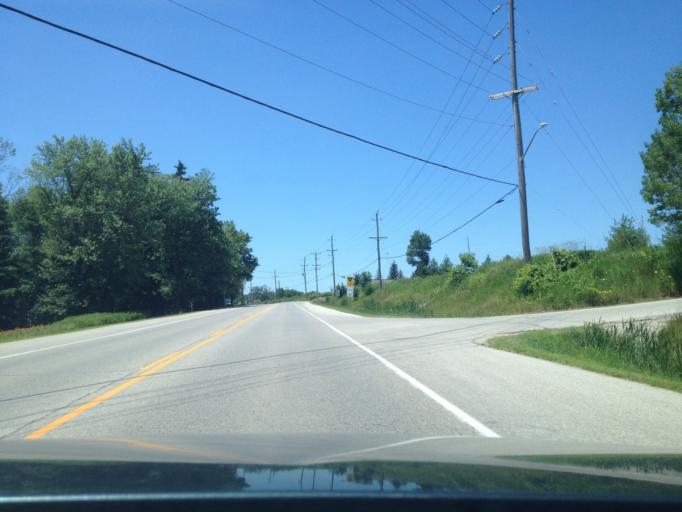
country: CA
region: Ontario
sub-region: Wellington County
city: Guelph
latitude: 43.6920
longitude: -80.4011
